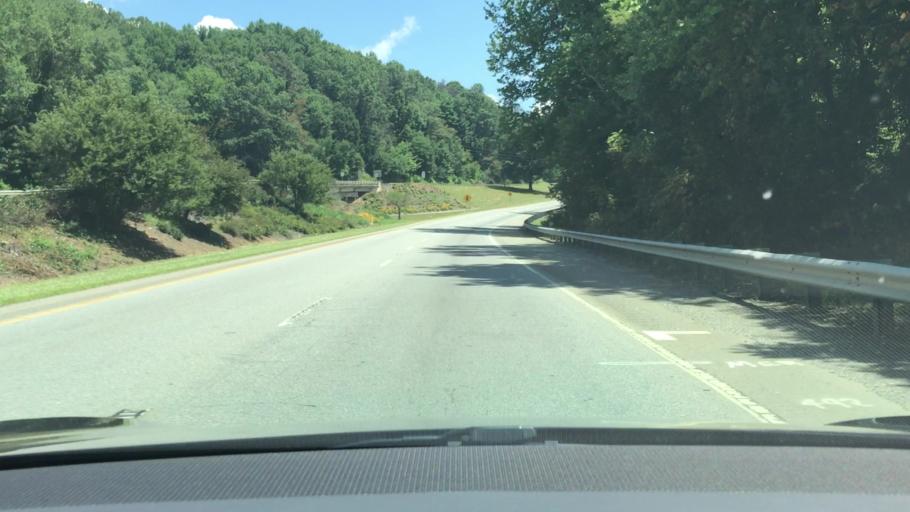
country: US
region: North Carolina
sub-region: Haywood County
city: Lake Junaluska
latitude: 35.5164
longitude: -82.9696
